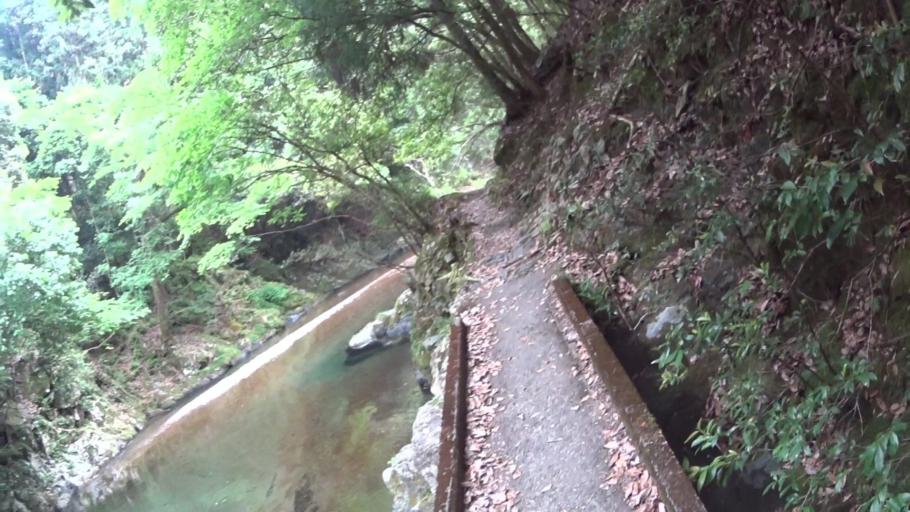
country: JP
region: Kyoto
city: Kameoka
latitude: 35.0325
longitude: 135.6519
